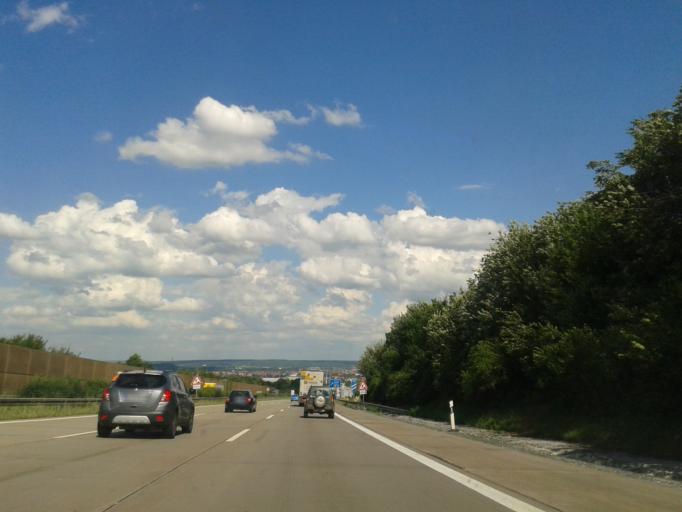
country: DE
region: Saxony
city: Radebeul
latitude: 51.0714
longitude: 13.6456
